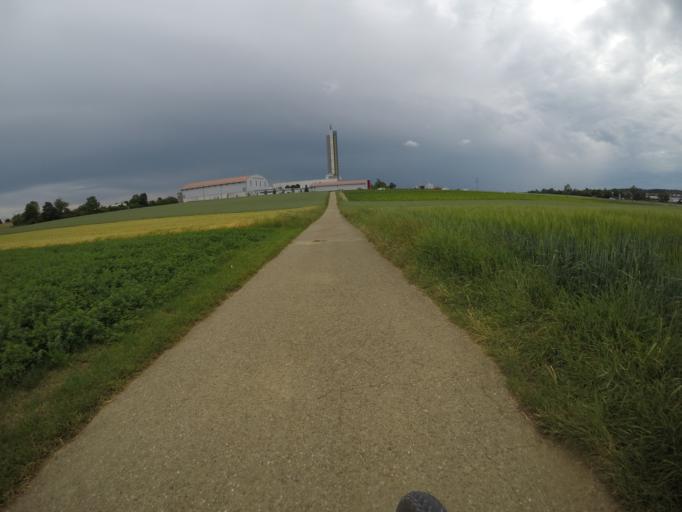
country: DE
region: Baden-Wuerttemberg
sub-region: Tuebingen Region
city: Ulm
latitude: 48.4371
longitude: 9.9815
